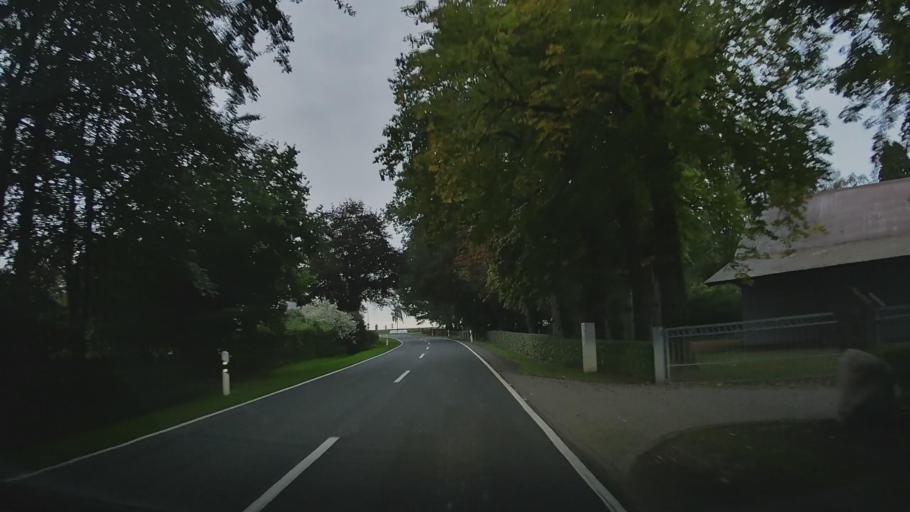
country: DE
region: Lower Saxony
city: Bassum
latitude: 52.8893
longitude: 8.7046
